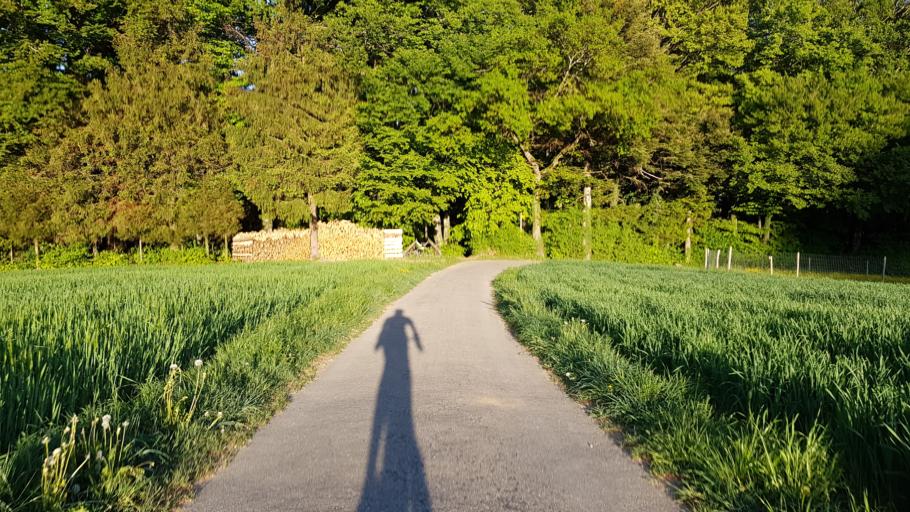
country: CH
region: Aargau
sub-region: Bezirk Kulm
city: Reinach
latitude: 47.2743
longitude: 8.1893
